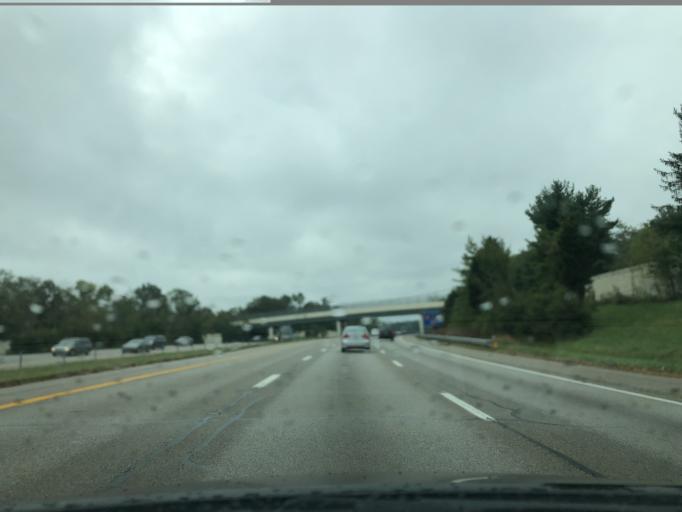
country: US
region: Ohio
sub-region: Hamilton County
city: The Village of Indian Hill
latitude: 39.2498
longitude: -84.3084
